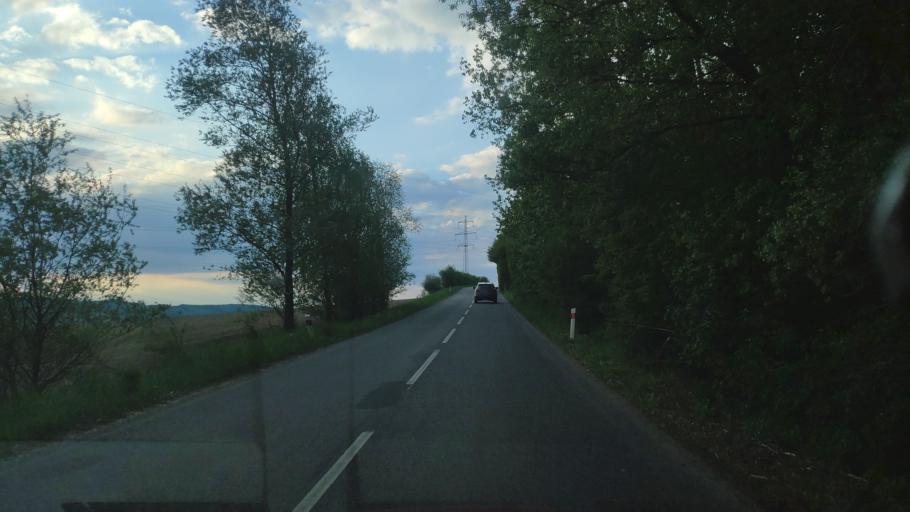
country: SK
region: Presovsky
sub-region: Okres Presov
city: Presov
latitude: 48.9026
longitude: 21.2622
